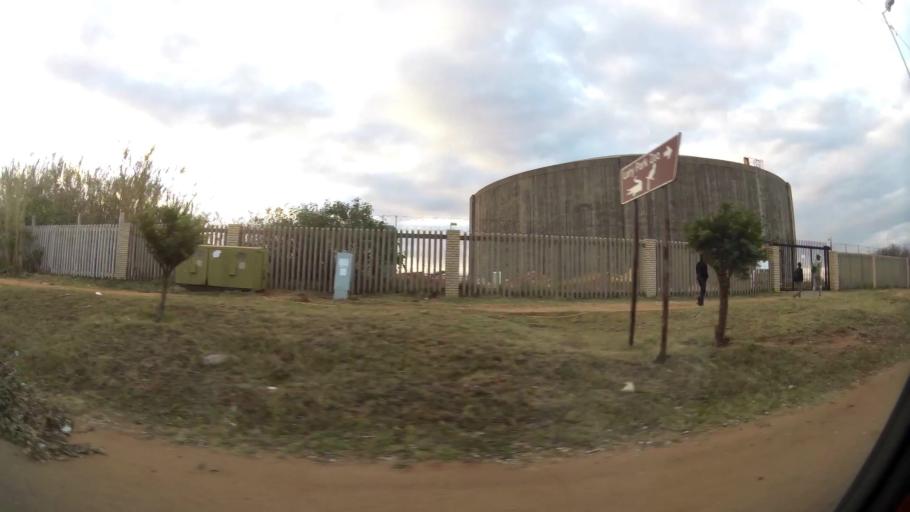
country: ZA
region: Gauteng
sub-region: City of Johannesburg Metropolitan Municipality
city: Midrand
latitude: -25.9937
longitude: 28.1472
